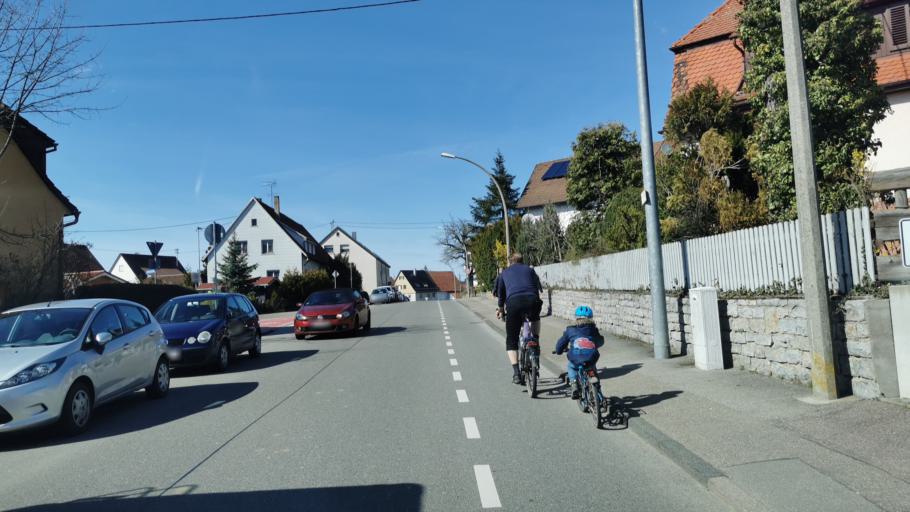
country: DE
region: Baden-Wuerttemberg
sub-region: Regierungsbezirk Stuttgart
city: Rutesheim
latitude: 48.8060
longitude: 8.9505
